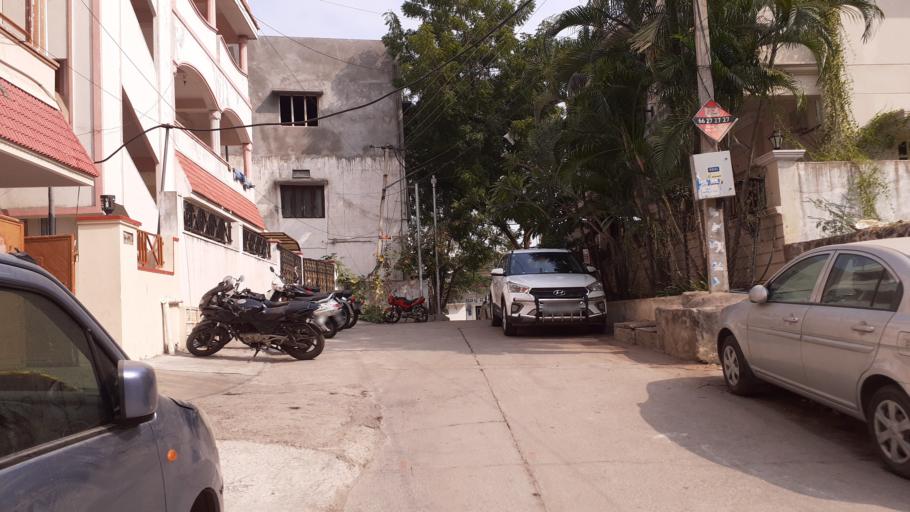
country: IN
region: Telangana
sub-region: Rangareddi
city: Kukatpalli
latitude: 17.4506
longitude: 78.4483
